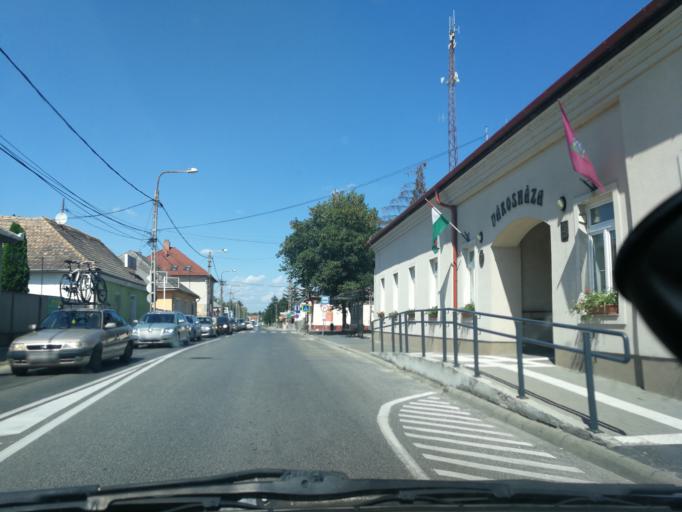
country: HU
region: Fejer
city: Martonvasar
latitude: 47.3148
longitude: 18.7895
